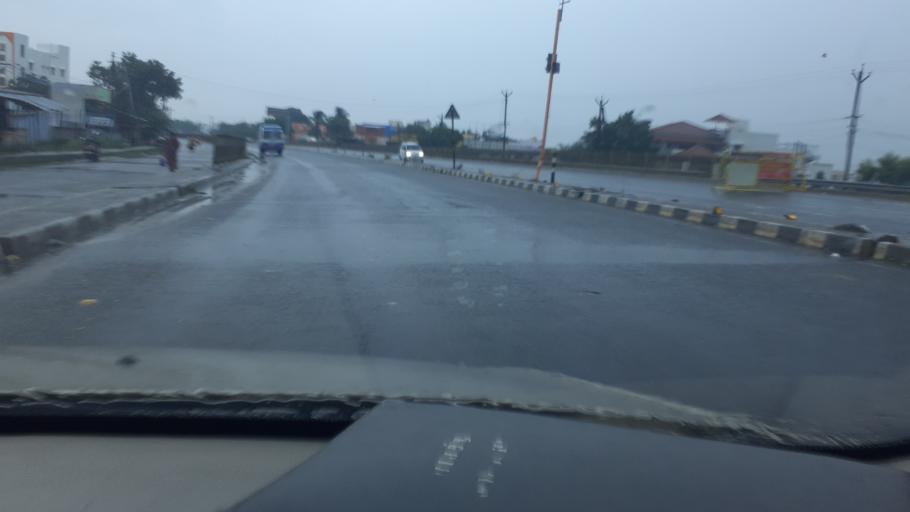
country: IN
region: Tamil Nadu
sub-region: Virudhunagar
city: Sattur
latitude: 9.3737
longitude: 77.9124
